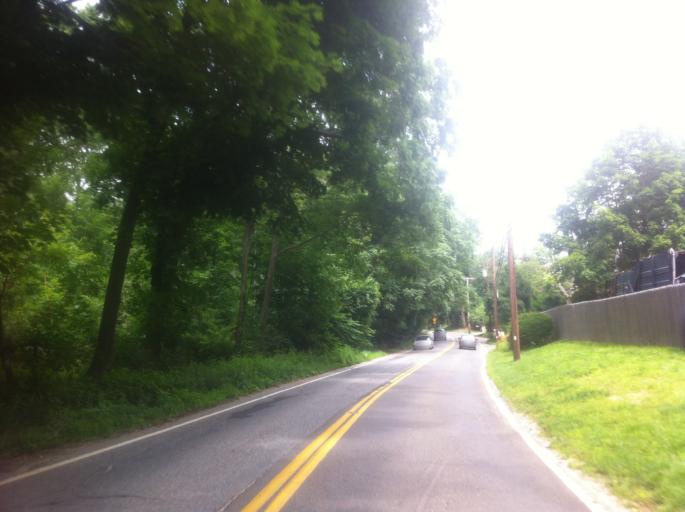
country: US
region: New York
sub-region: Nassau County
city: Locust Valley
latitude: 40.8772
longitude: -73.6138
